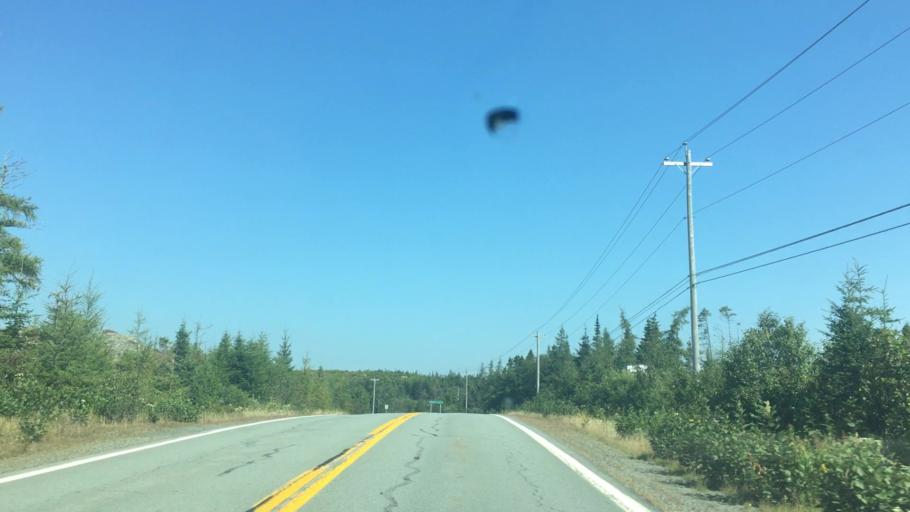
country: CA
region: Nova Scotia
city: Antigonish
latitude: 45.0199
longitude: -62.0322
